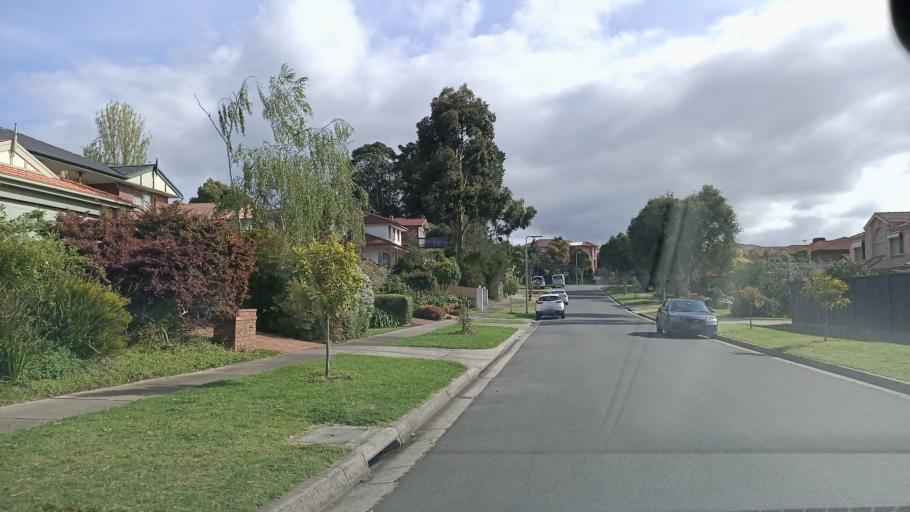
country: AU
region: Victoria
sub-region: Monash
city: Mulgrave
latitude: -37.9266
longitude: 145.1977
